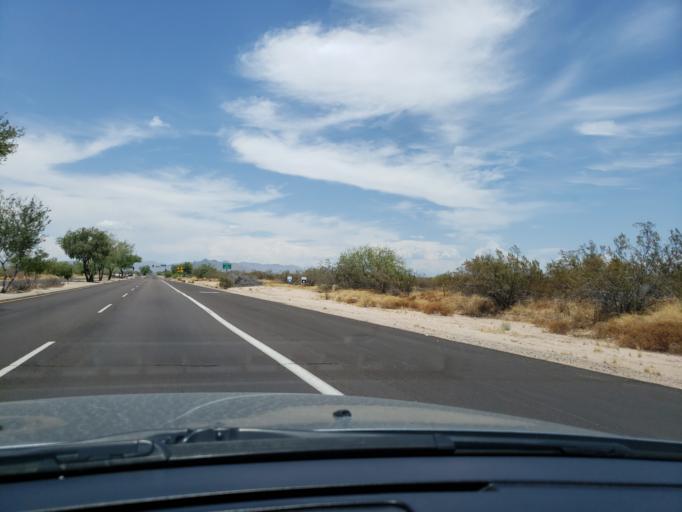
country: US
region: Arizona
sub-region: Maricopa County
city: Cave Creek
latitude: 33.7241
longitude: -112.0098
